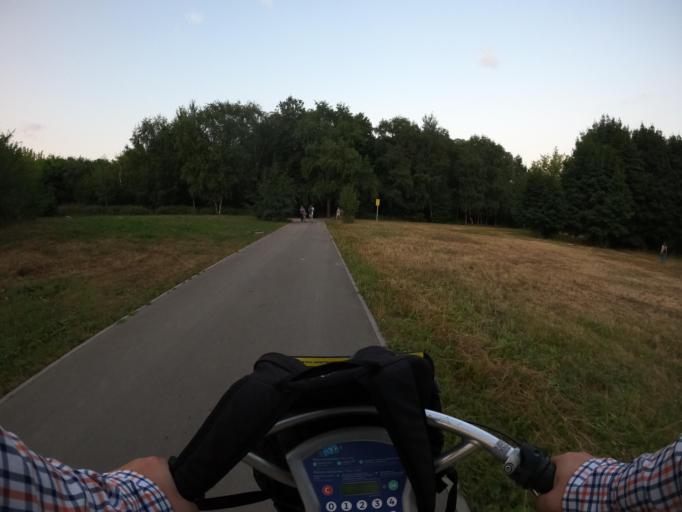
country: RU
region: Moscow
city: Lyublino
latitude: 55.6897
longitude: 37.7598
